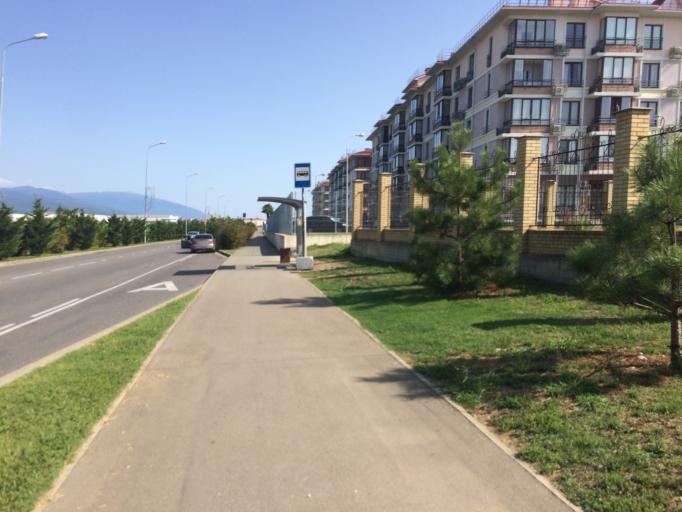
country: RU
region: Krasnodarskiy
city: Adler
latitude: 43.3981
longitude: 39.9760
